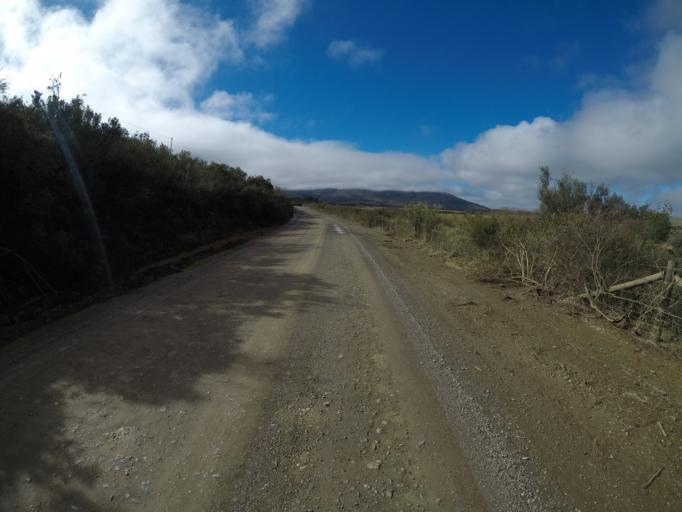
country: ZA
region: Western Cape
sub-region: Cape Winelands District Municipality
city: Ashton
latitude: -34.1232
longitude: 19.8318
